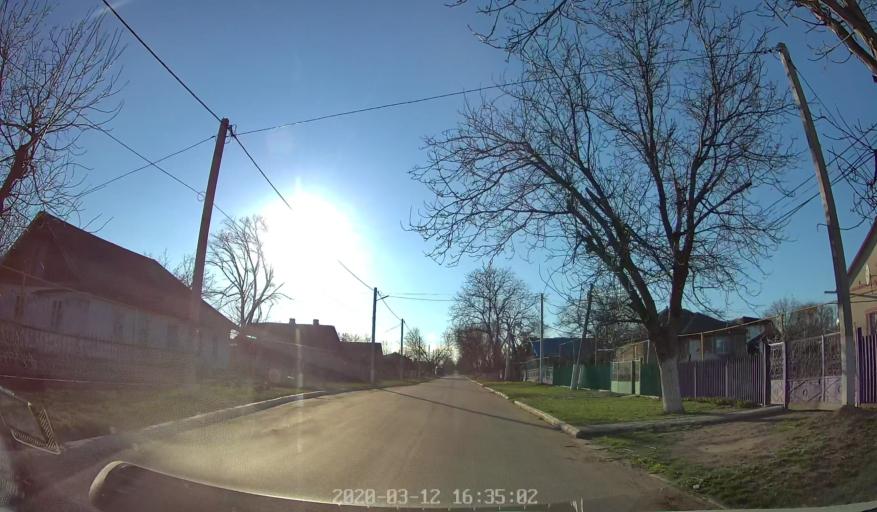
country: MD
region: Anenii Noi
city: Anenii Noi
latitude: 46.8137
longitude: 29.2028
